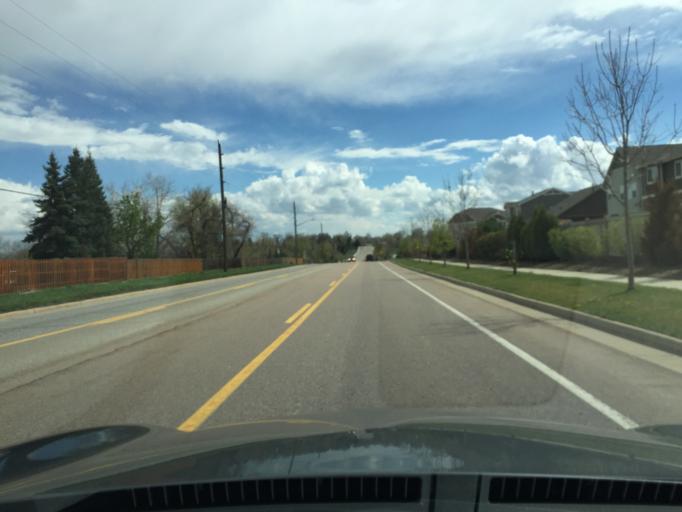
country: US
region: Colorado
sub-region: Boulder County
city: Lafayette
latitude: 40.0062
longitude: -105.0933
